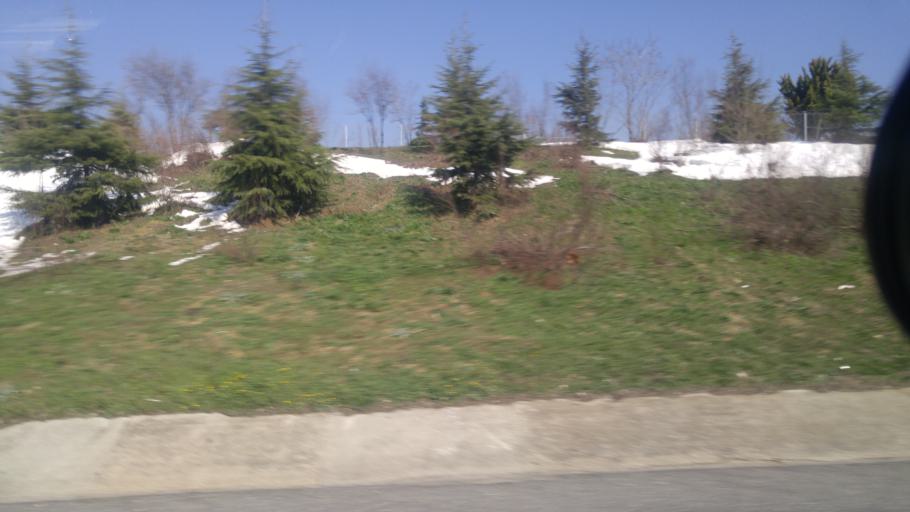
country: TR
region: Istanbul
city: Celaliye
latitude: 41.0612
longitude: 28.4094
